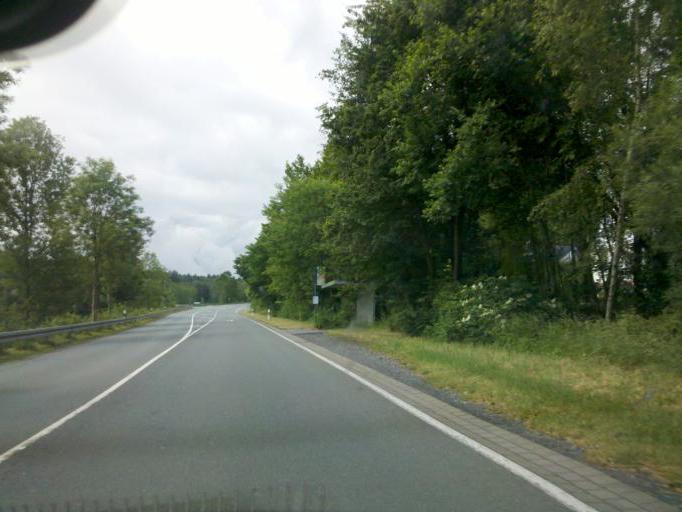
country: DE
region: North Rhine-Westphalia
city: Warstein
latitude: 51.4230
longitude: 8.3420
